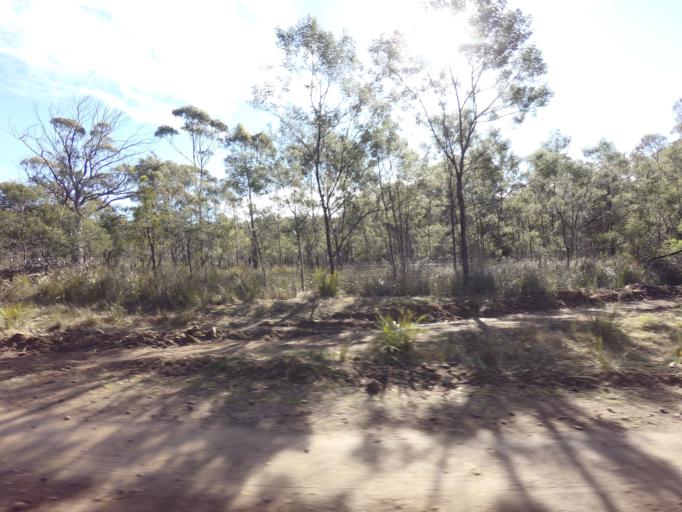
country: AU
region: Tasmania
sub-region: Sorell
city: Sorell
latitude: -42.4051
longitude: 147.9647
